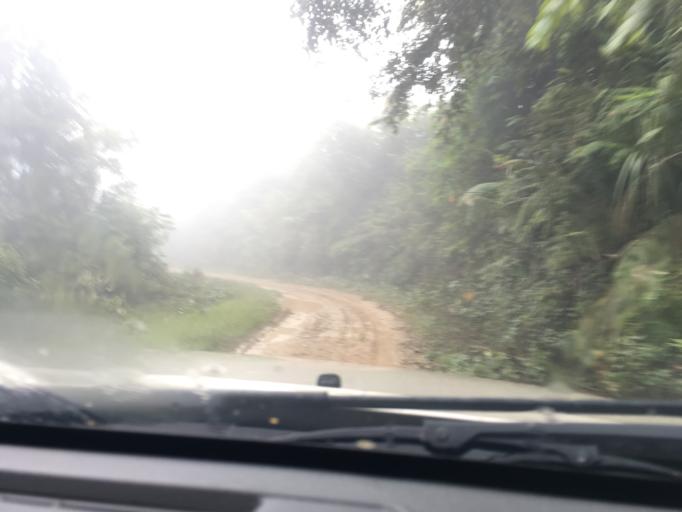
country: LA
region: Phongsali
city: Phongsali
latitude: 21.4288
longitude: 102.2618
